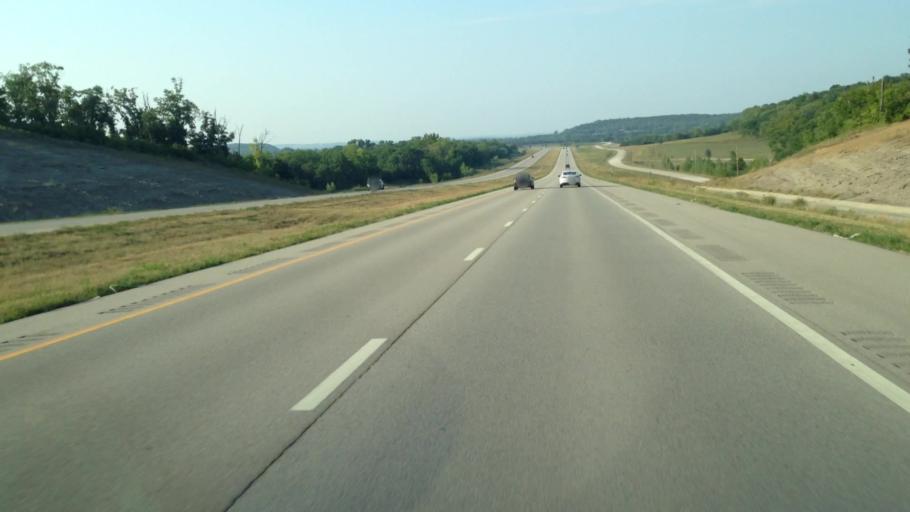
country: US
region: Kansas
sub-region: Douglas County
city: Baldwin City
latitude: 38.8548
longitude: -95.2628
